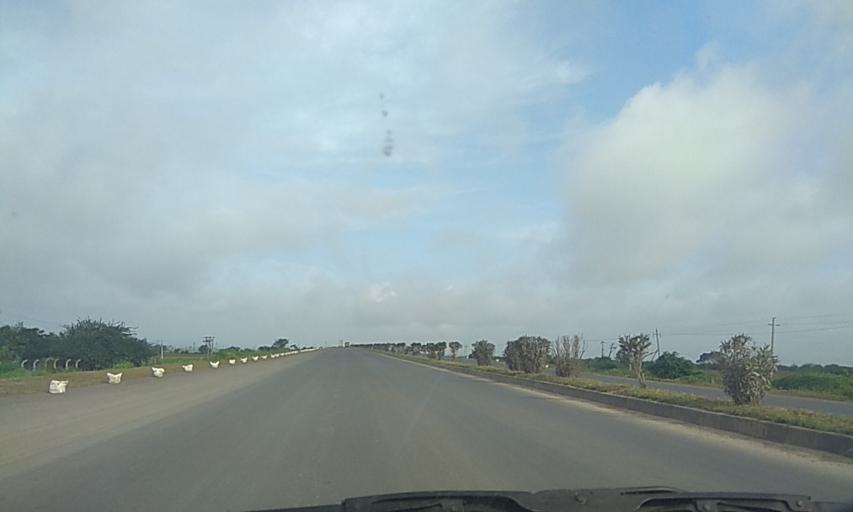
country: IN
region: Karnataka
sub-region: Haveri
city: Haveri
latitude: 14.8353
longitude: 75.3571
